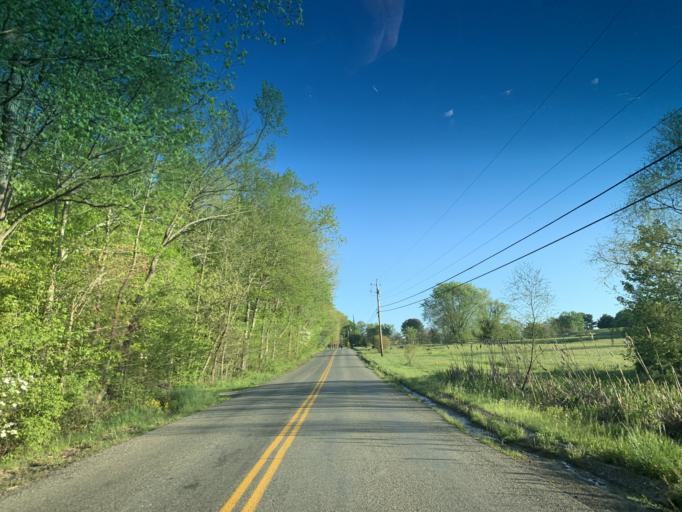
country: US
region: Maryland
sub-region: Harford County
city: Aberdeen
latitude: 39.5439
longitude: -76.1788
